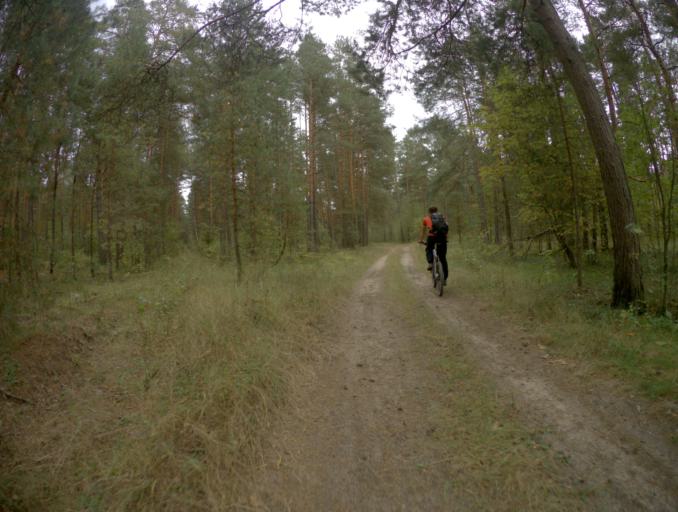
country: RU
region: Vladimir
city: Raduzhnyy
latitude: 56.0320
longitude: 40.3766
